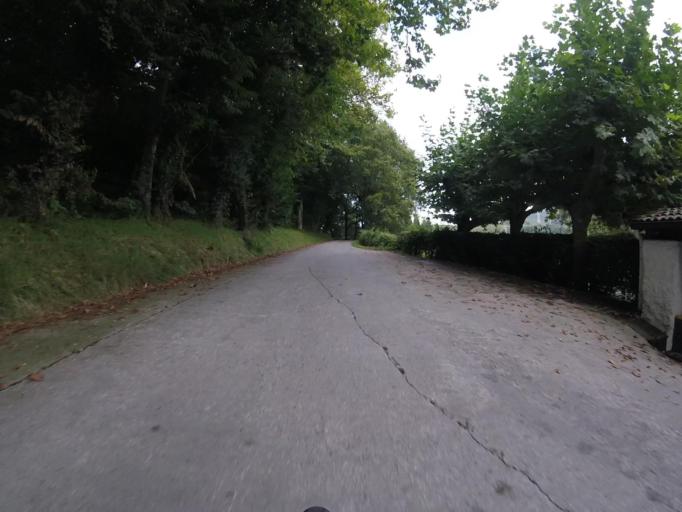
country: ES
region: Basque Country
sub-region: Provincia de Guipuzcoa
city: Lezo
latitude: 43.3033
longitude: -1.8545
